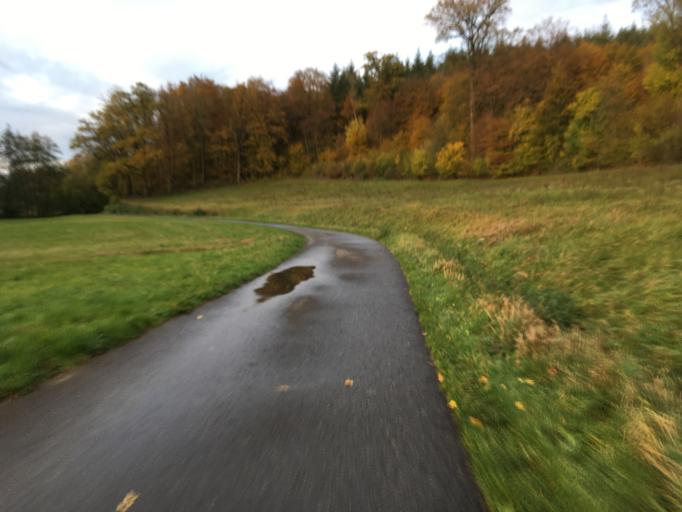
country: DE
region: Baden-Wuerttemberg
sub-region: Regierungsbezirk Stuttgart
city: Jagsthausen
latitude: 49.3754
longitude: 9.4995
